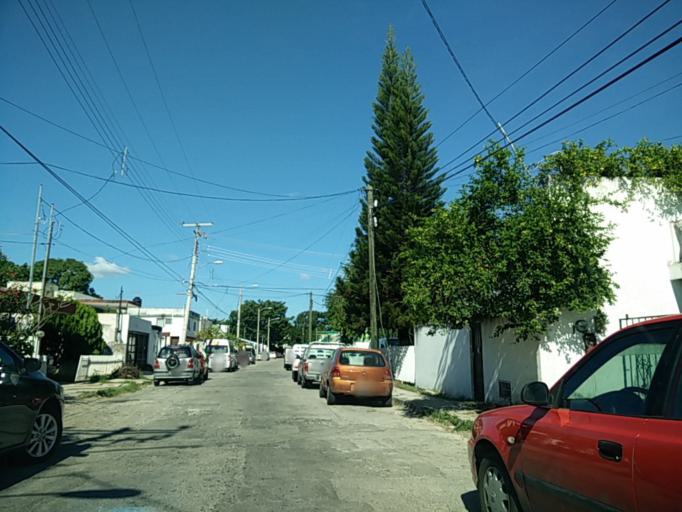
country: MX
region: Yucatan
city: Merida
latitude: 20.9892
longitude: -89.6100
